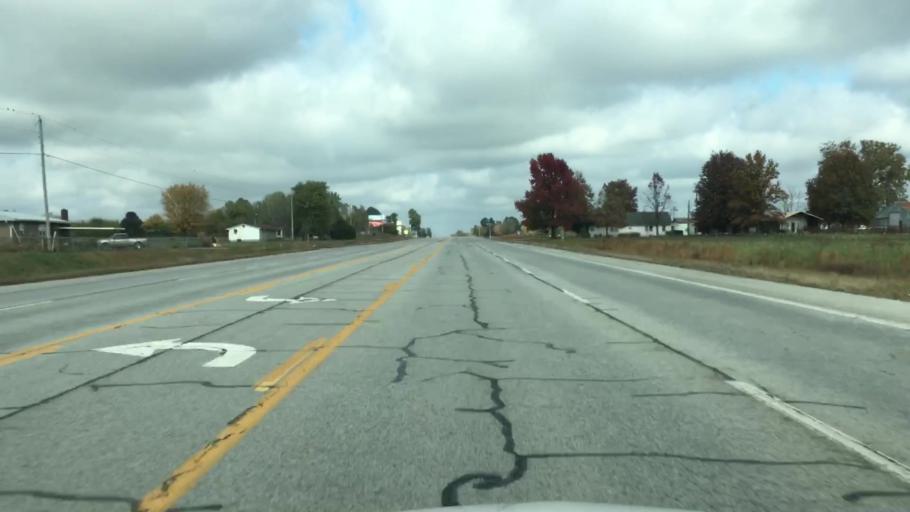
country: US
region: Arkansas
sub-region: Benton County
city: Gentry
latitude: 36.2172
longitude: -94.4954
